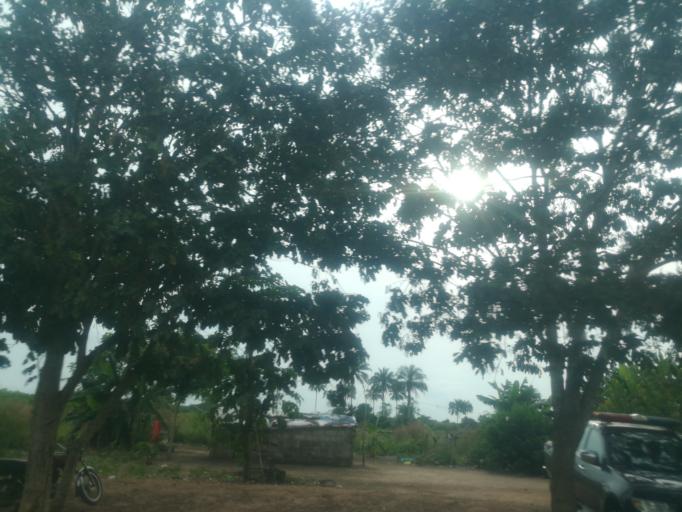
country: NG
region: Ogun
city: Ayetoro
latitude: 7.2500
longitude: 3.1186
